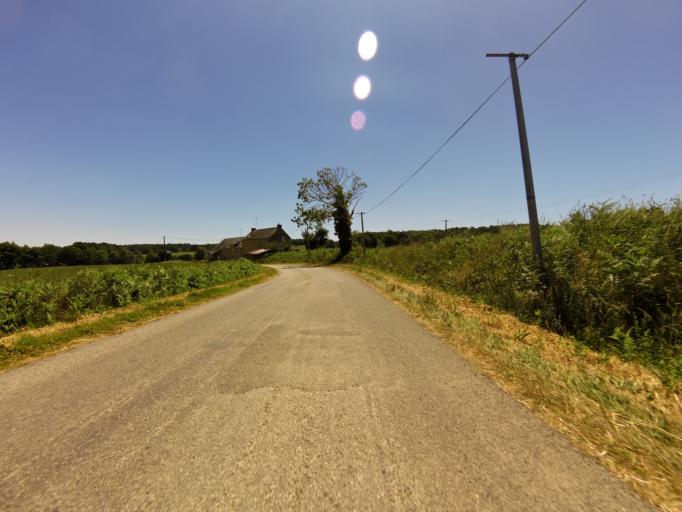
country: FR
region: Brittany
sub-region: Departement du Morbihan
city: Molac
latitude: 47.7117
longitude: -2.4084
